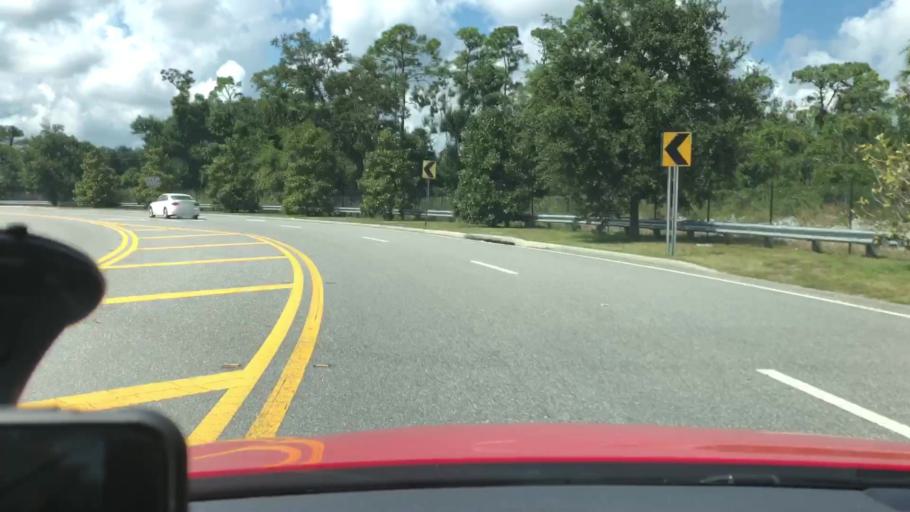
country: US
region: Florida
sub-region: Volusia County
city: Port Orange
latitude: 29.1116
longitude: -81.0233
